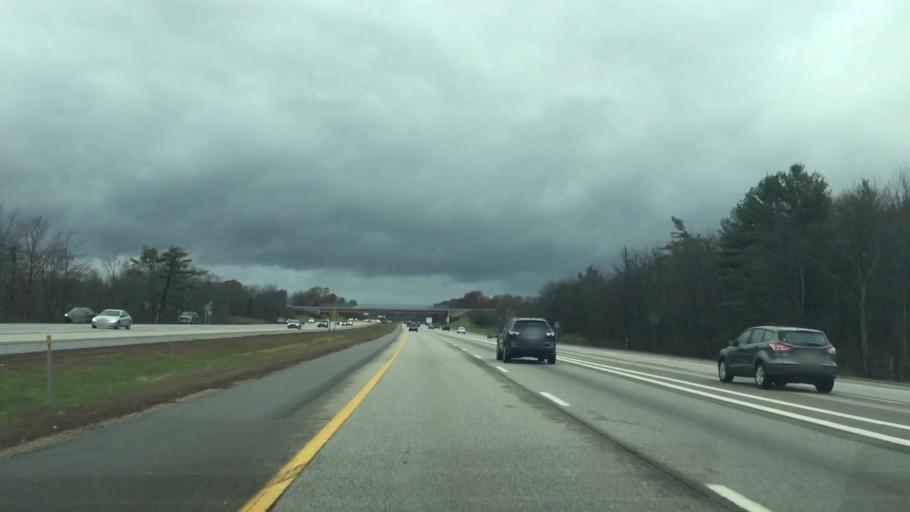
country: US
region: New Hampshire
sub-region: Rockingham County
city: North Hampton
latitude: 42.9696
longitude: -70.8548
